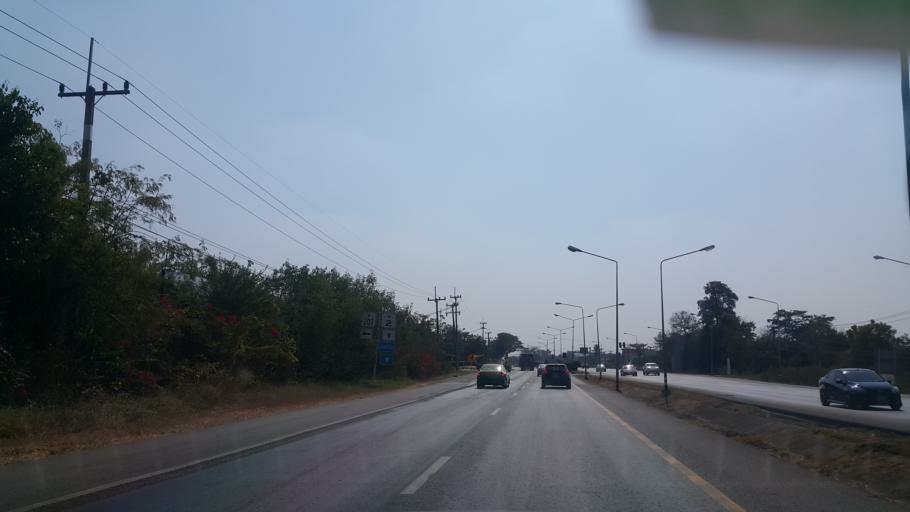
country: TH
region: Nakhon Ratchasima
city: Non Daeng
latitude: 15.3498
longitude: 102.4466
